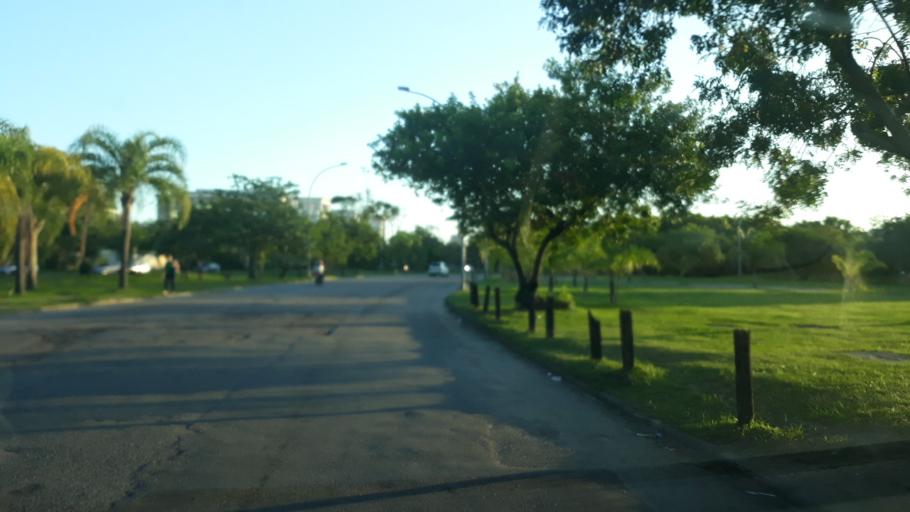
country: BR
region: Rio de Janeiro
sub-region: Rio De Janeiro
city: Rio de Janeiro
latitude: -22.9858
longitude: -43.3602
